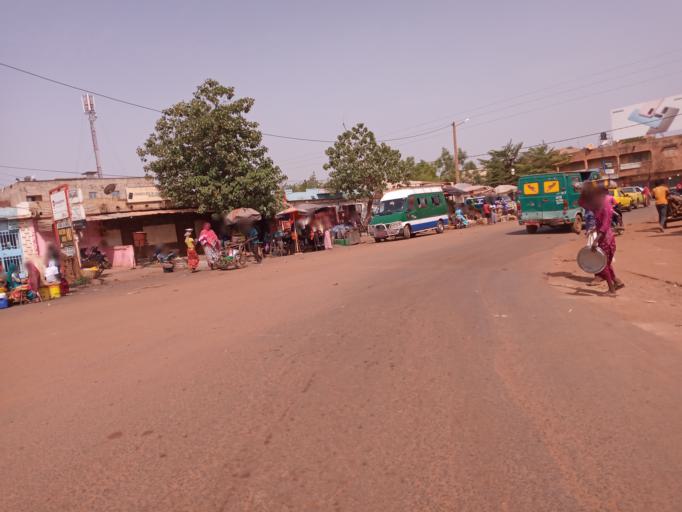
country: ML
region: Bamako
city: Bamako
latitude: 12.6076
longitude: -8.0057
